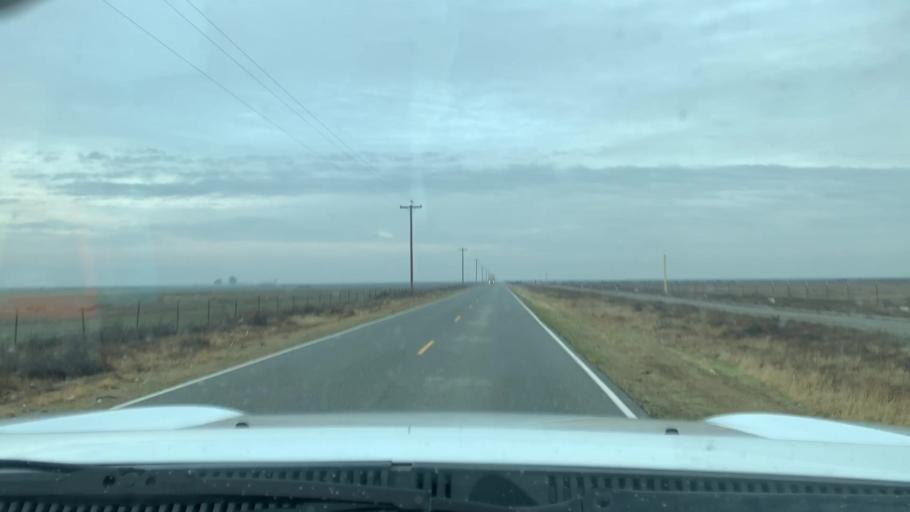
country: US
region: California
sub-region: Kern County
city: Lost Hills
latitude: 35.6713
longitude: -119.5799
